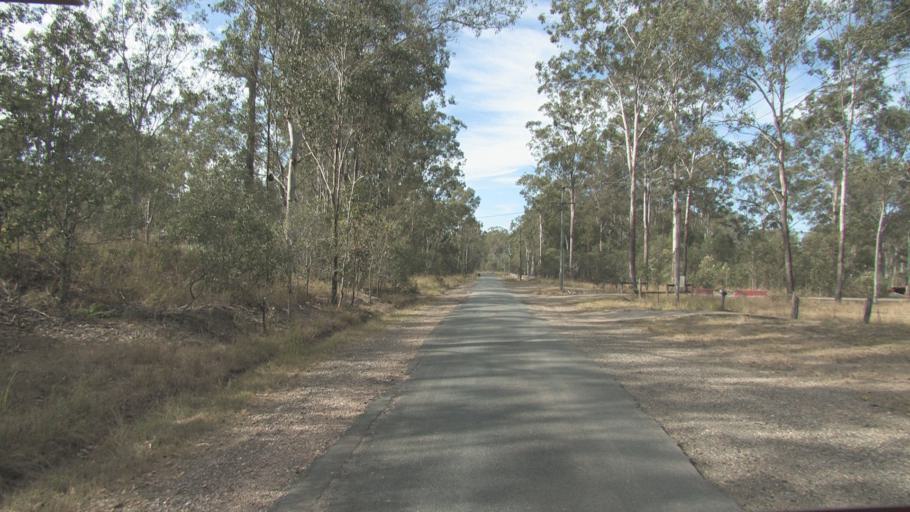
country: AU
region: Queensland
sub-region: Logan
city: North Maclean
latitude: -27.7480
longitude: 152.9788
